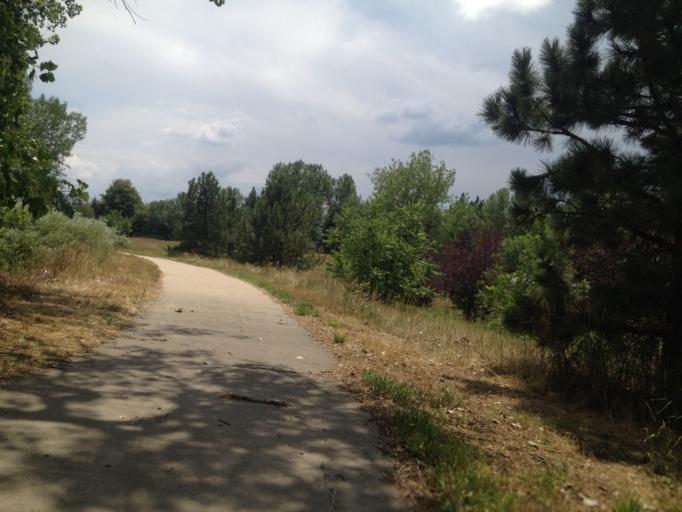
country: US
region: Colorado
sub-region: Boulder County
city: Louisville
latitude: 39.9663
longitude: -105.1499
